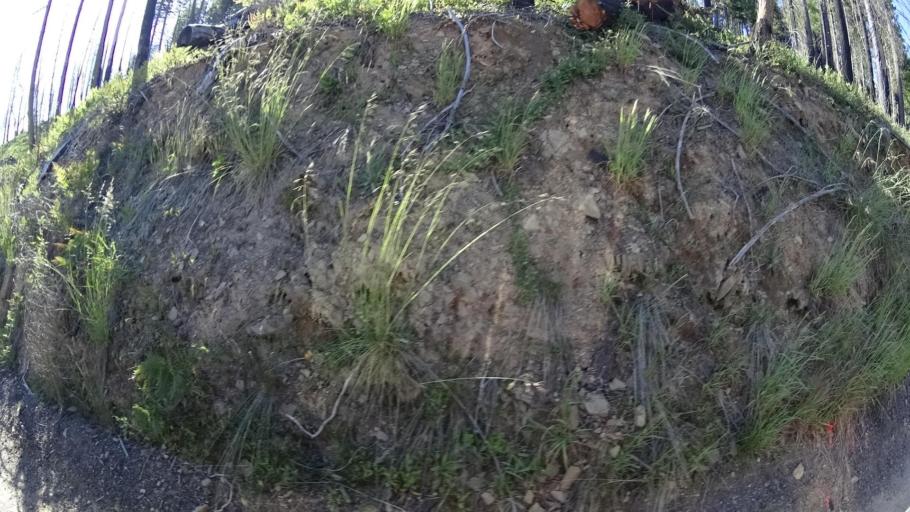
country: US
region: California
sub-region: Lake County
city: Upper Lake
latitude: 39.3779
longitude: -122.9901
